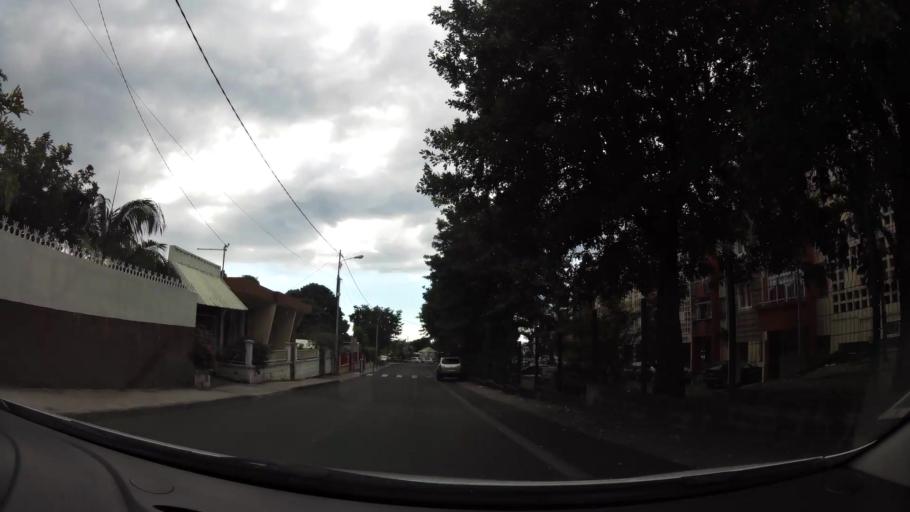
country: RE
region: Reunion
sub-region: Reunion
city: Saint-Denis
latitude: -20.8907
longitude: 55.4743
